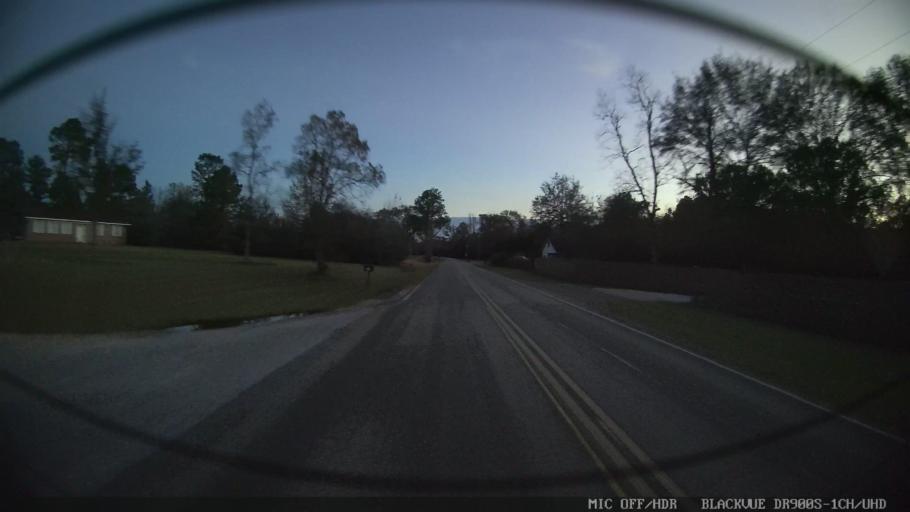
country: US
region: Mississippi
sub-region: Forrest County
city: Hattiesburg
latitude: 31.1711
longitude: -89.2182
